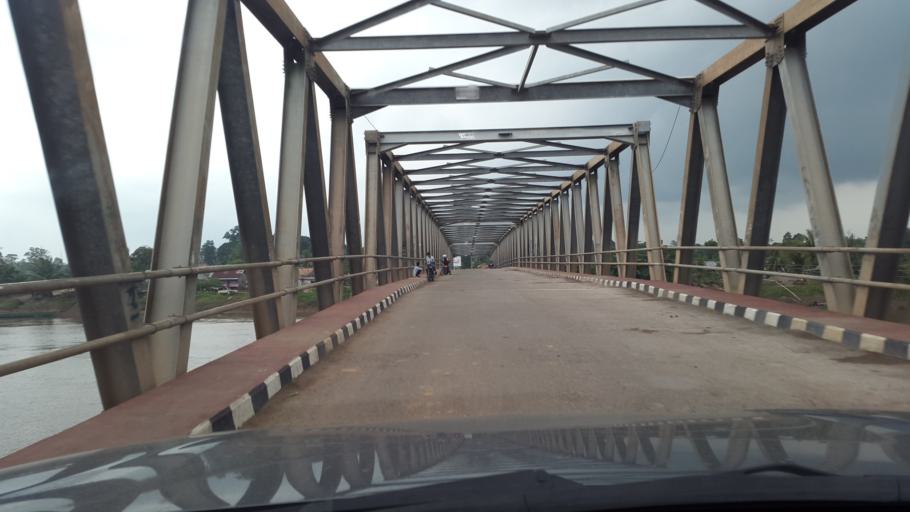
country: ID
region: South Sumatra
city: Sekayu
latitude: -2.8704
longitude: 103.8286
